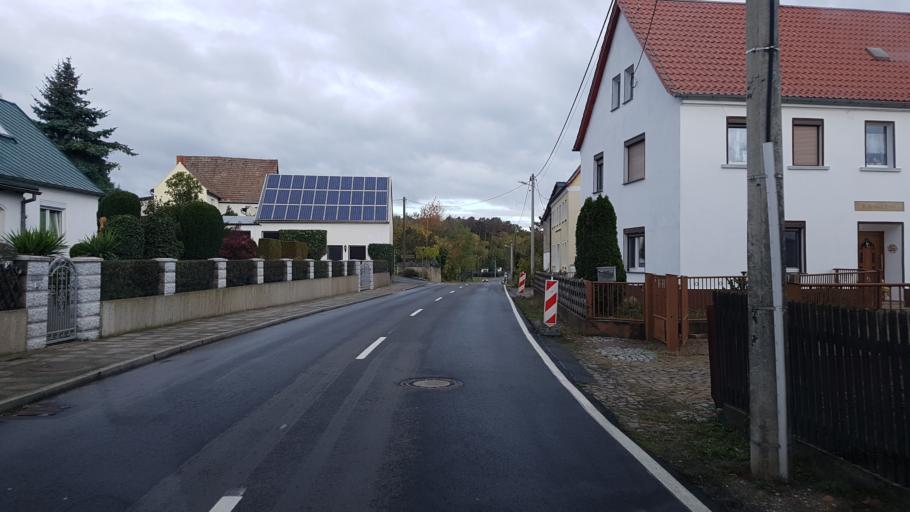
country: DE
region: Saxony
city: Dahlen
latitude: 51.3991
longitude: 12.9829
